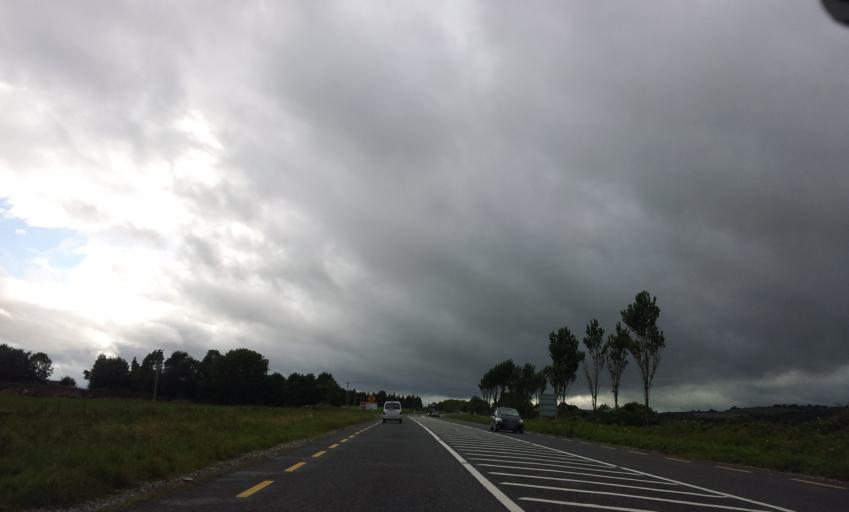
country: IE
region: Munster
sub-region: County Cork
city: Youghal
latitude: 51.9391
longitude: -7.9234
